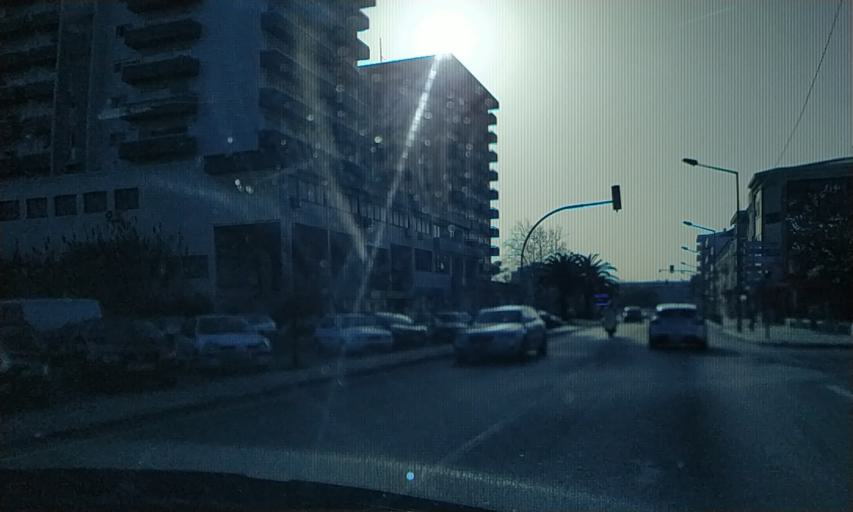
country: PT
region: Leiria
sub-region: Marinha Grande
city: Marinha Grande
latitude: 39.7476
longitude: -8.9303
